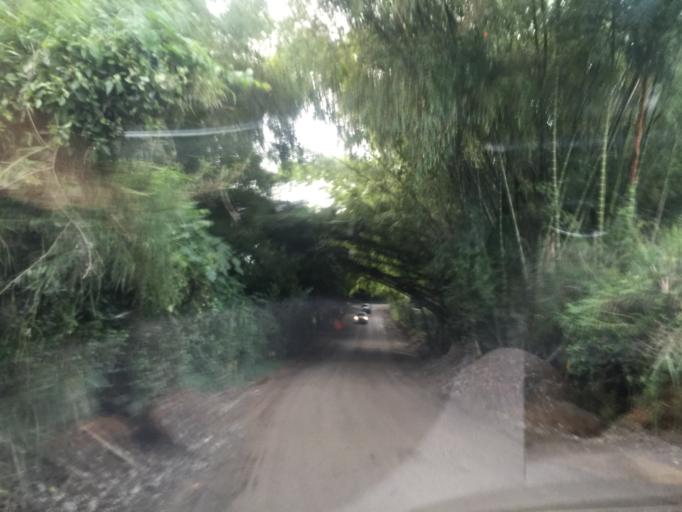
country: CO
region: Quindio
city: La Tebaida
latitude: 4.4595
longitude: -75.7998
